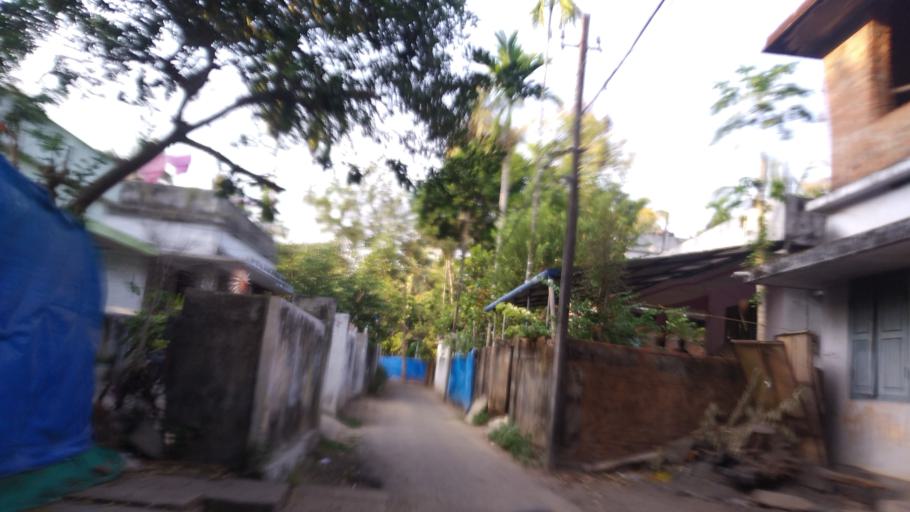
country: IN
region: Kerala
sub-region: Ernakulam
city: Elur
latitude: 10.0877
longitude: 76.2117
